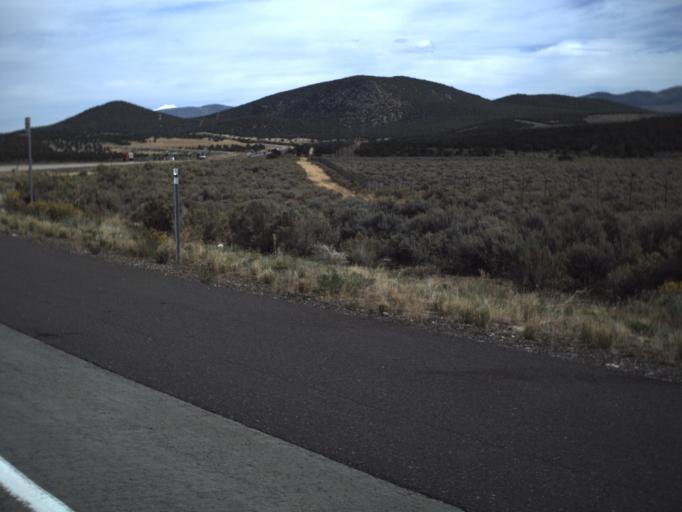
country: US
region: Utah
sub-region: Beaver County
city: Beaver
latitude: 38.1317
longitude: -112.6253
